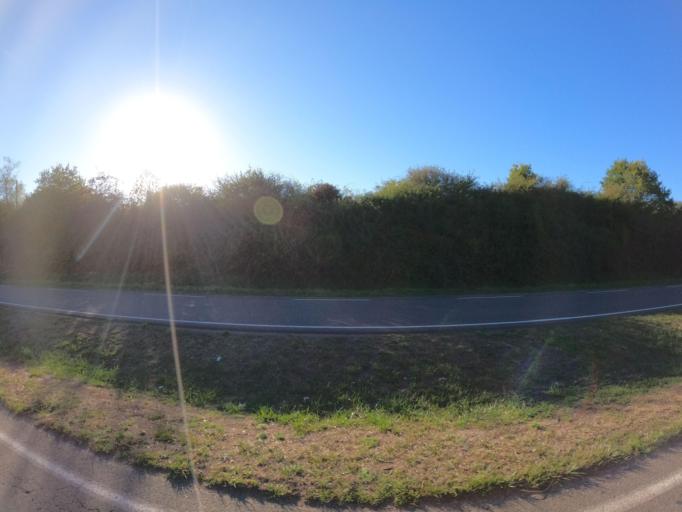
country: FR
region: Bourgogne
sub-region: Departement de Saone-et-Loire
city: Torcy
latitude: 46.7643
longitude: 4.4441
